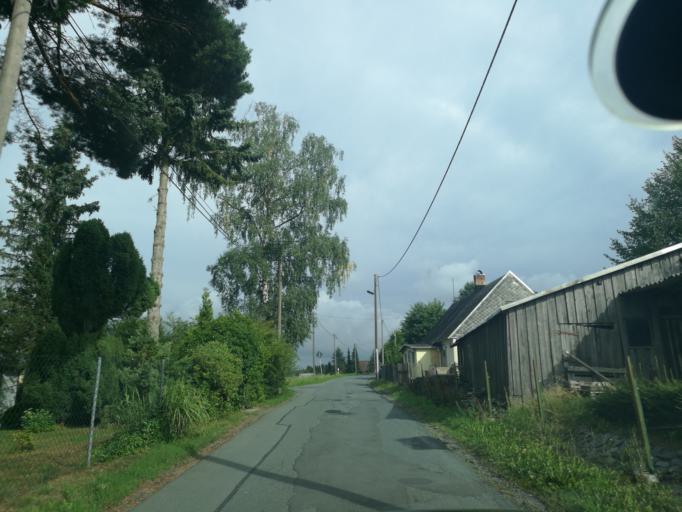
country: DE
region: Saxony
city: Adorf
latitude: 50.3076
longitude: 12.2754
